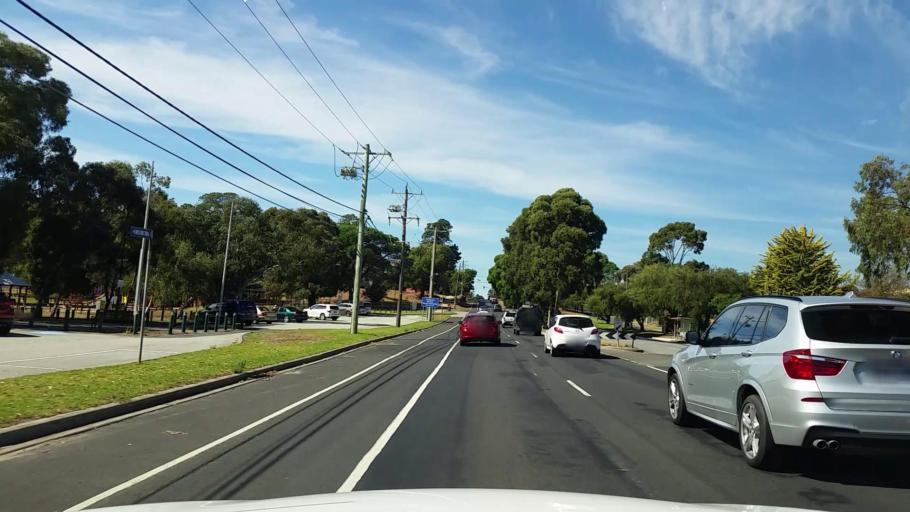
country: AU
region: Victoria
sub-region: Frankston
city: Langwarrin
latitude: -38.1530
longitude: 145.1583
